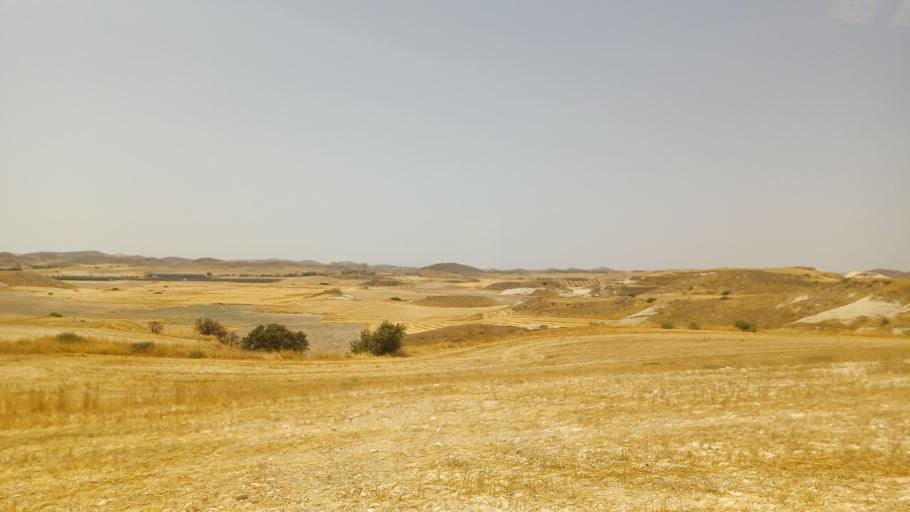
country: CY
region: Larnaka
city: Troulloi
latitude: 35.0377
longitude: 33.5933
